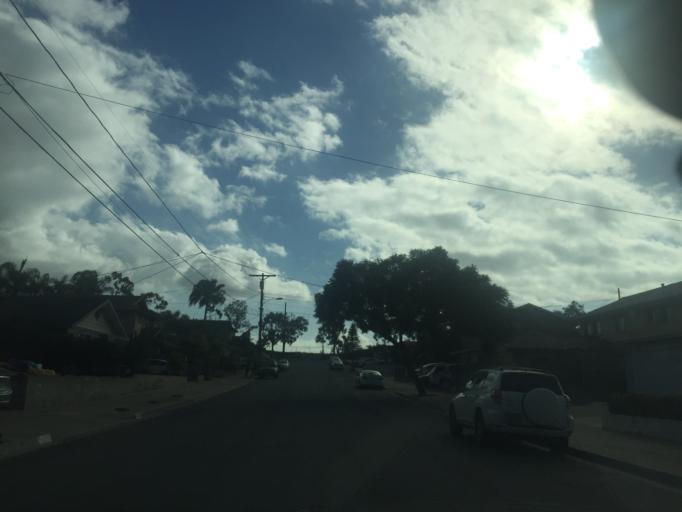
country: US
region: California
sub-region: San Diego County
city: San Diego
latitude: 32.7814
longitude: -117.1515
